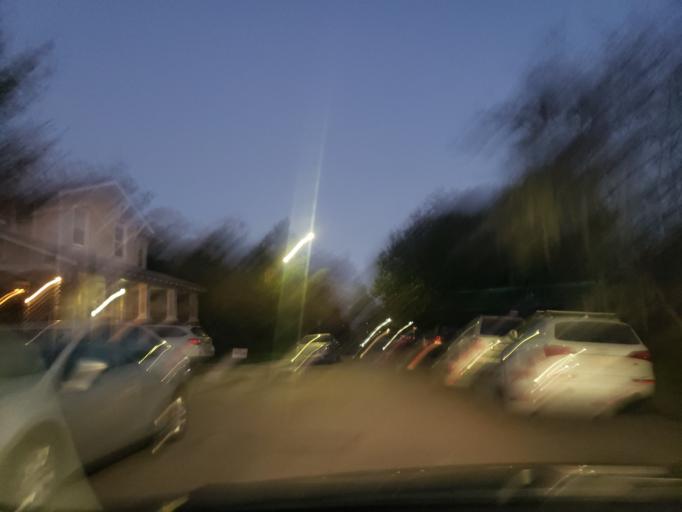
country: US
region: Georgia
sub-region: Chatham County
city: Savannah
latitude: 32.0514
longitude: -81.0929
